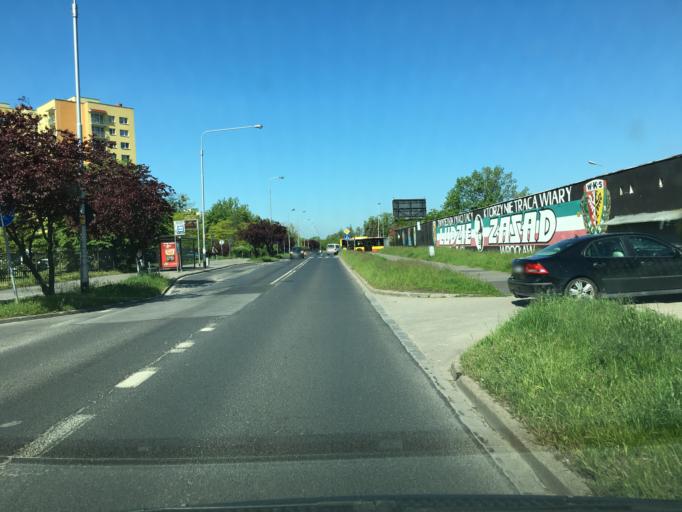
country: PL
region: Lower Silesian Voivodeship
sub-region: Powiat wroclawski
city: Wroclaw
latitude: 51.1187
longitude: 16.9544
